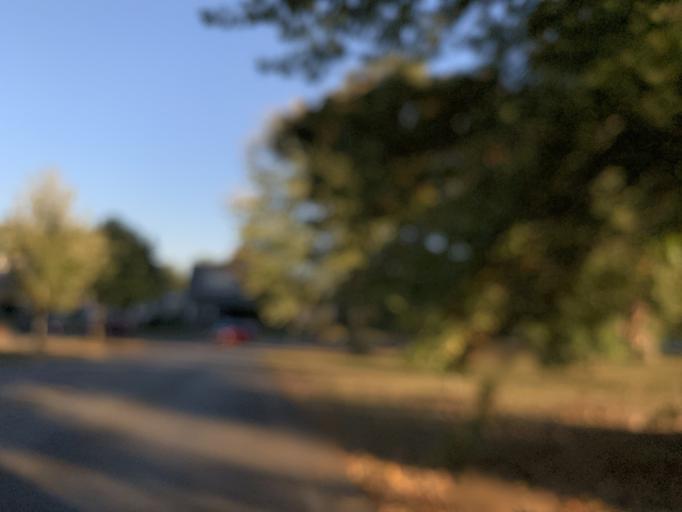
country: US
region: Indiana
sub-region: Floyd County
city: New Albany
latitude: 38.2603
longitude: -85.8245
